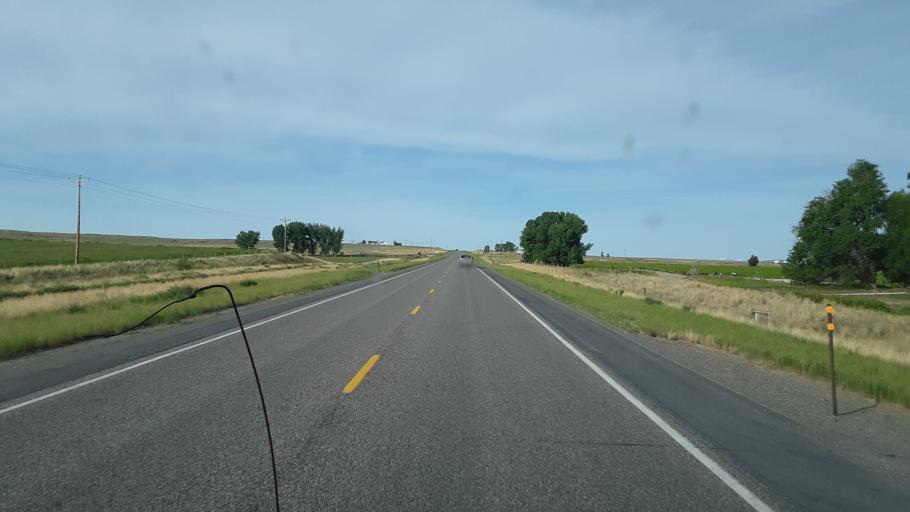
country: US
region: Wyoming
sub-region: Fremont County
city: Riverton
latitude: 43.1701
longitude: -108.2603
